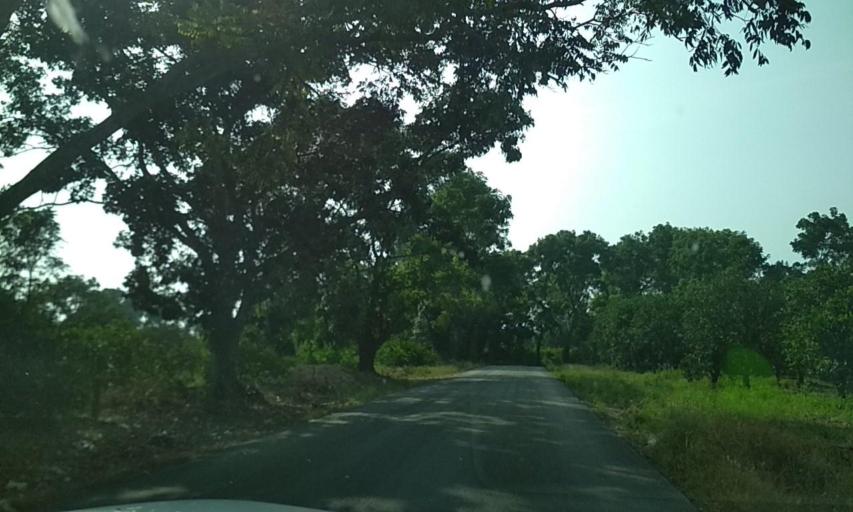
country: MX
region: Veracruz
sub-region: Martinez de la Torre
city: El Progreso
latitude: 20.1508
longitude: -97.0669
